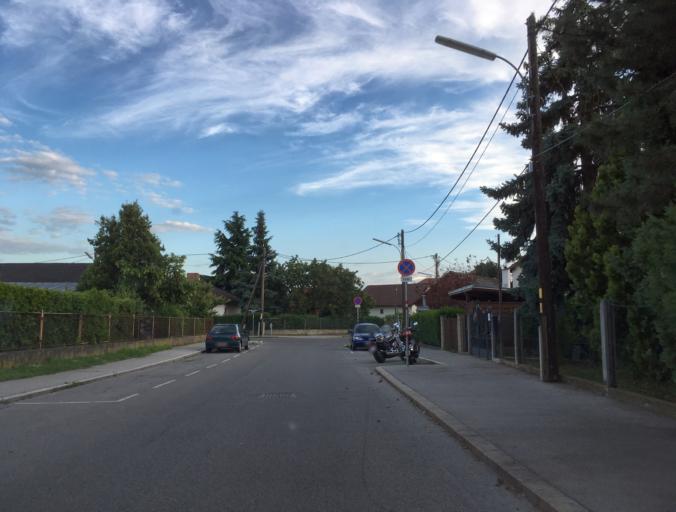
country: AT
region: Vienna
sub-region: Wien Stadt
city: Vienna
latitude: 48.2451
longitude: 16.4007
